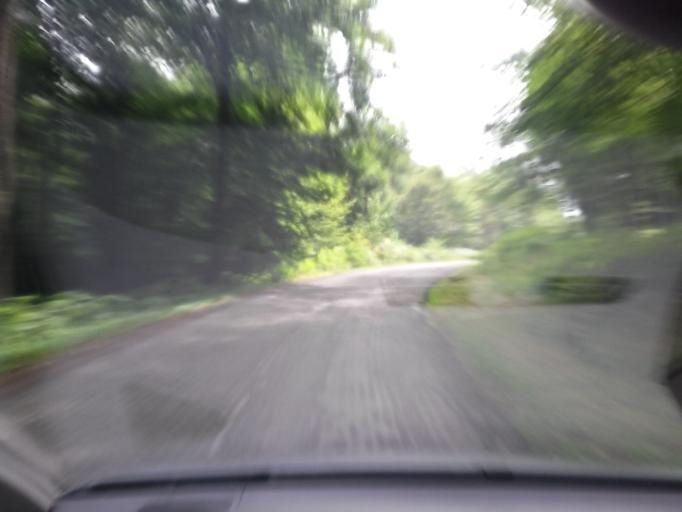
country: BE
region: Wallonia
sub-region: Province du Luxembourg
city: Chiny
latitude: 49.7522
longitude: 5.3106
